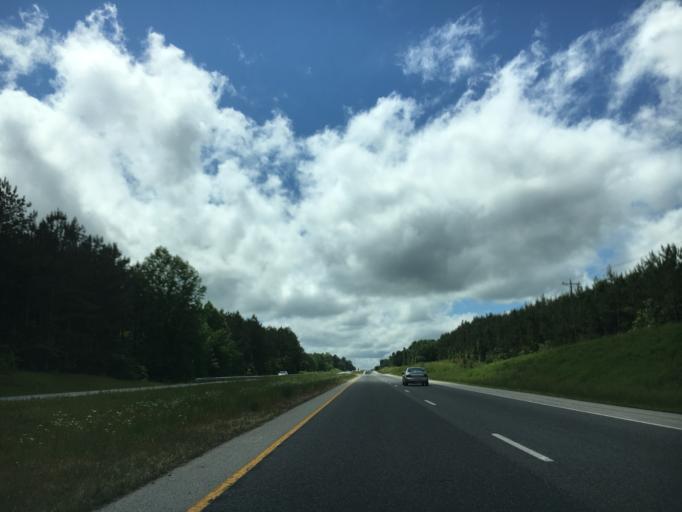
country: US
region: Virginia
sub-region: Mecklenburg County
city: Bracey
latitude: 36.6713
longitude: -78.2431
